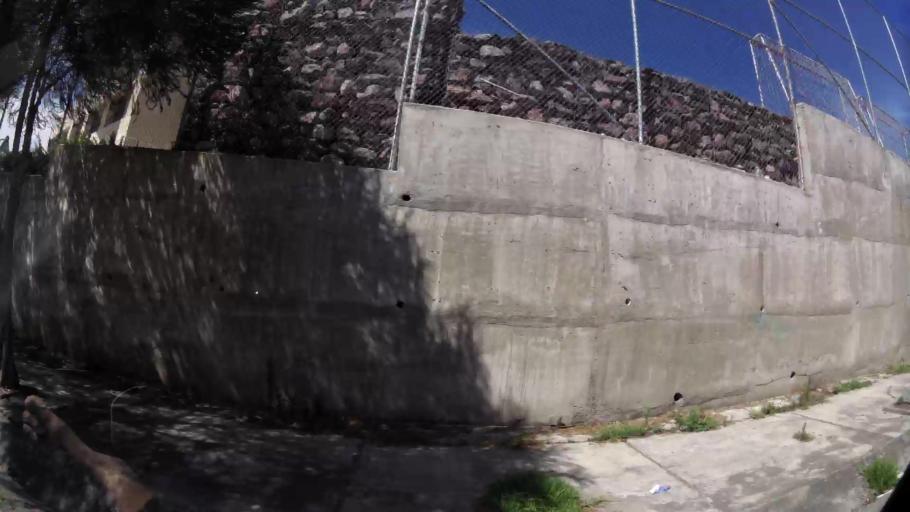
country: EC
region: Pichincha
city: Quito
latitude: -0.1965
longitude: -78.4428
